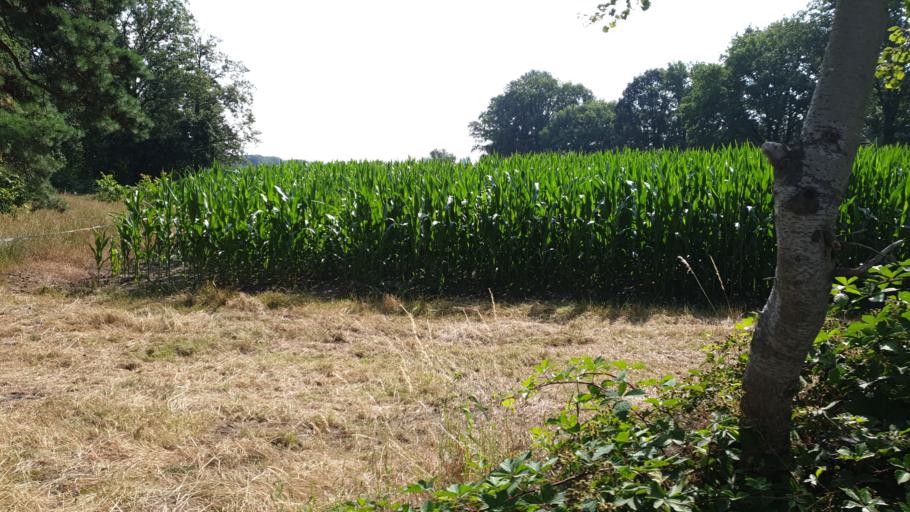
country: BE
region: Flanders
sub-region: Provincie Antwerpen
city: Geel
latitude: 51.1844
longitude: 5.0106
